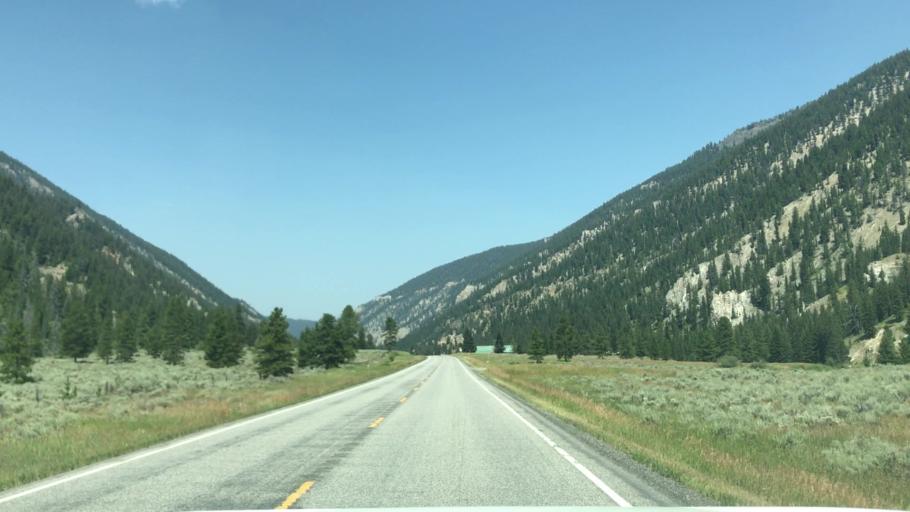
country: US
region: Montana
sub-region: Gallatin County
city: Big Sky
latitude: 45.1112
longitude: -111.2239
